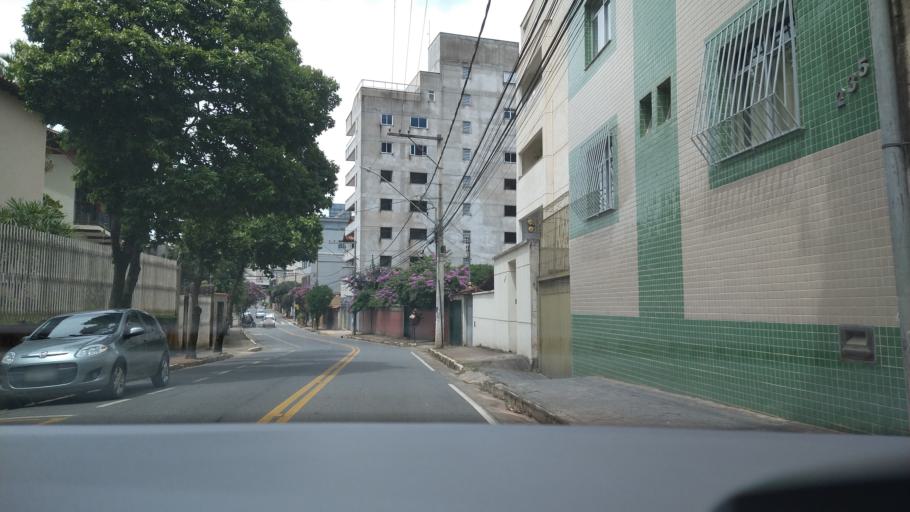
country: BR
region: Minas Gerais
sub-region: Vicosa
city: Vicosa
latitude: -20.7619
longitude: -42.8821
